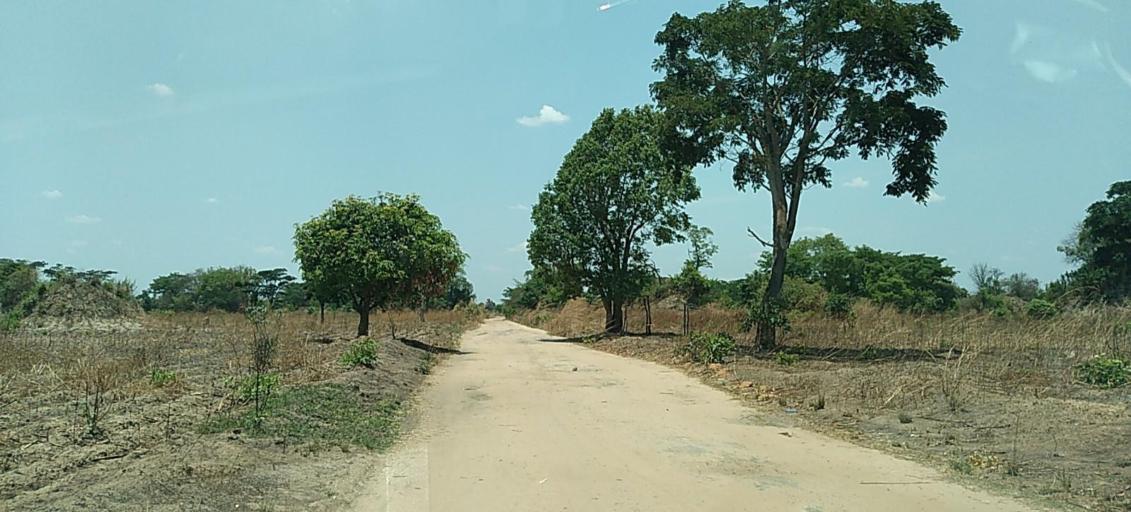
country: ZM
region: Copperbelt
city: Luanshya
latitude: -13.0808
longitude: 28.4053
